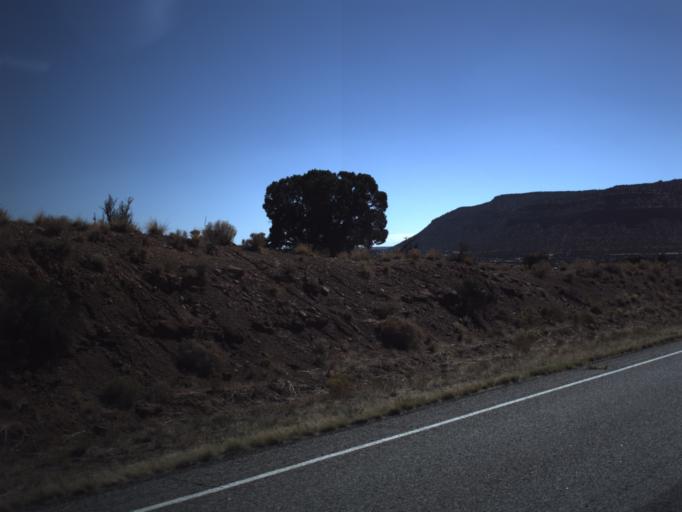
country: US
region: Utah
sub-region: San Juan County
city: Blanding
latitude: 37.6203
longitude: -110.0844
